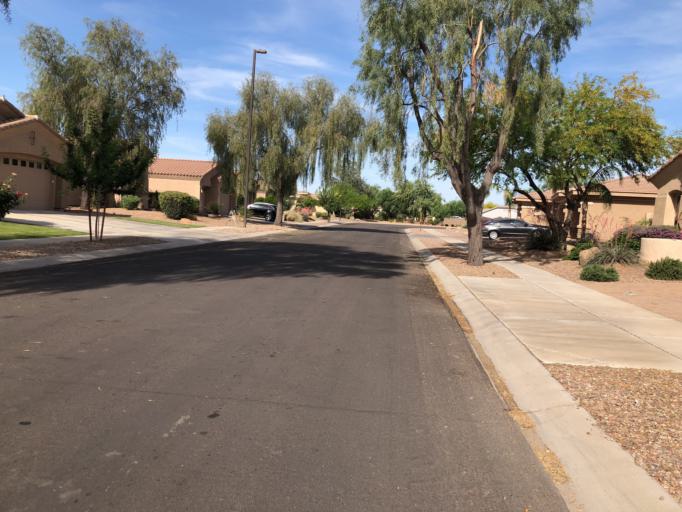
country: US
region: Arizona
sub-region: Maricopa County
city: Queen Creek
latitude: 33.2747
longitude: -111.6927
